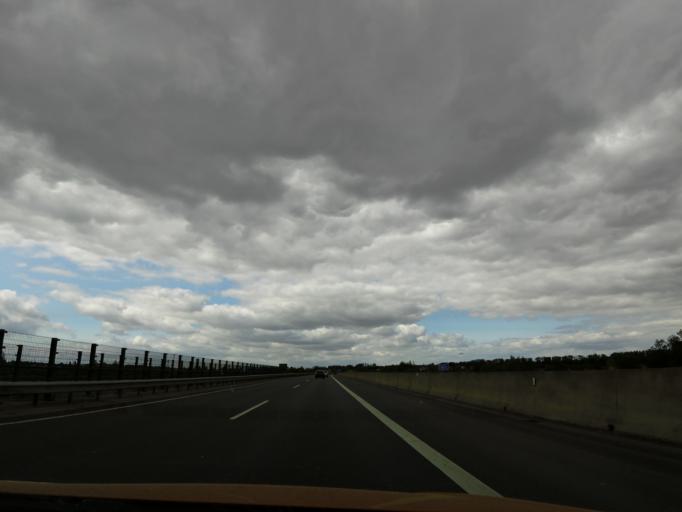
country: DE
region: Lower Saxony
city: Cremlingen
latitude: 52.2486
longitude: 10.5914
